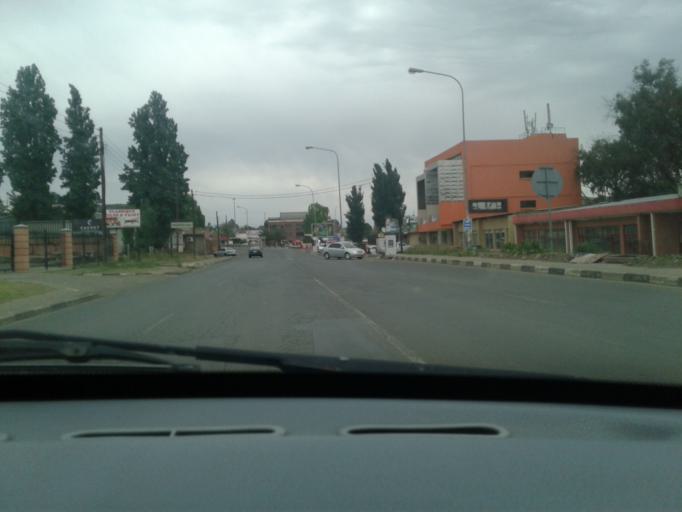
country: LS
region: Maseru
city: Maseru
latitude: -29.2988
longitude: 27.4711
